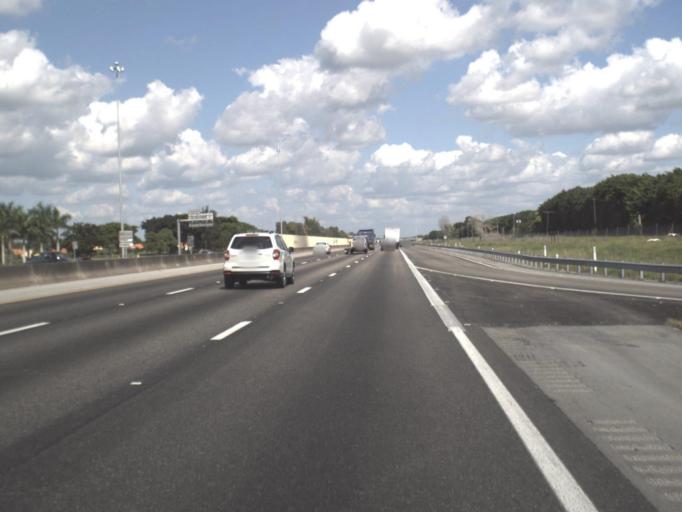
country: US
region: Florida
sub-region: Palm Beach County
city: Boca Del Mar
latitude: 26.3757
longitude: -80.1708
